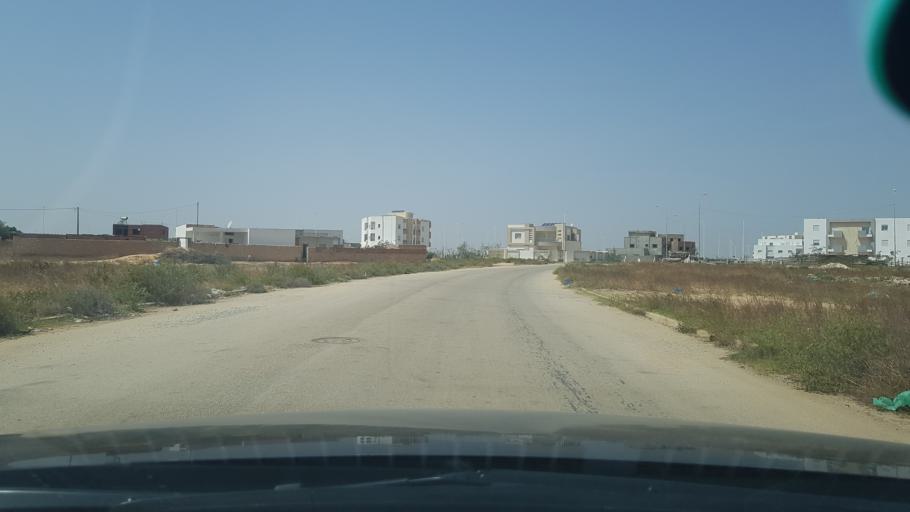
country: TN
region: Safaqis
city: Al Qarmadah
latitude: 34.8296
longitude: 10.7509
